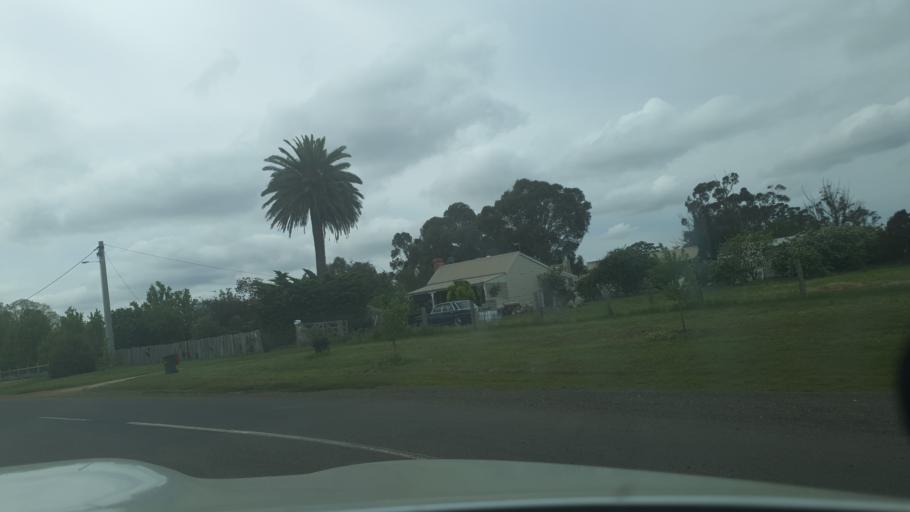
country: AU
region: Victoria
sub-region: Central Goldfields
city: Maryborough
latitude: -37.1783
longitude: 143.7059
